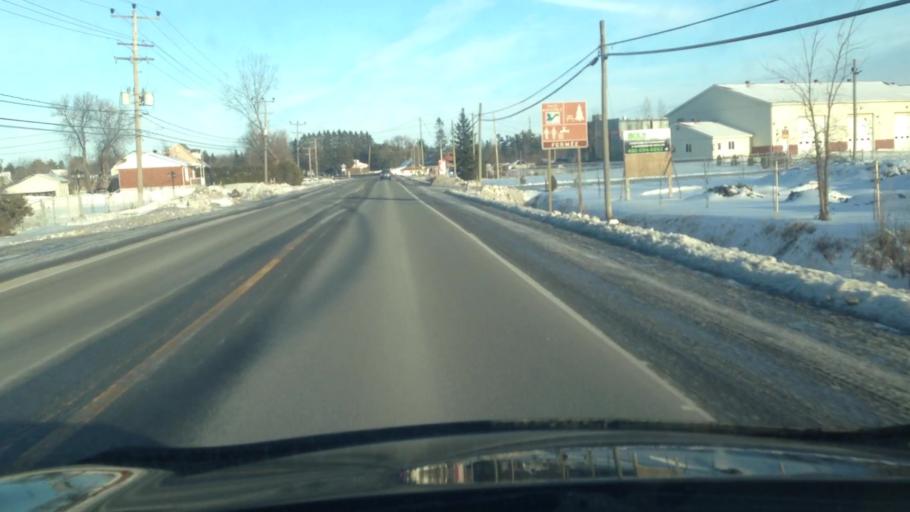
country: CA
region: Quebec
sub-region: Laurentides
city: Sainte-Sophie
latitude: 45.8107
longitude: -73.9204
